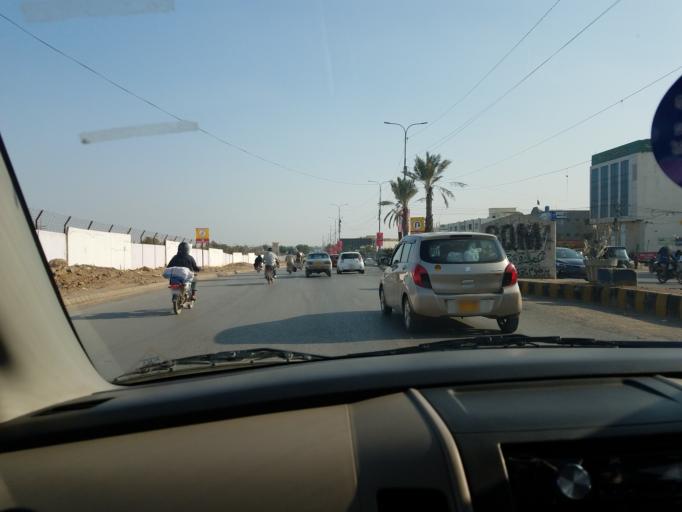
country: PK
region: Sindh
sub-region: Karachi District
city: Karachi
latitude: 24.8975
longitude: 67.1181
